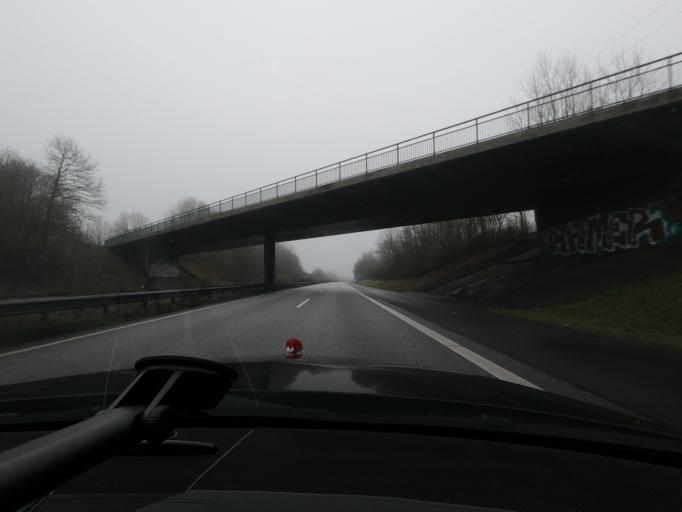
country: DE
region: Schleswig-Holstein
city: Dannewerk
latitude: 54.4946
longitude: 9.5194
